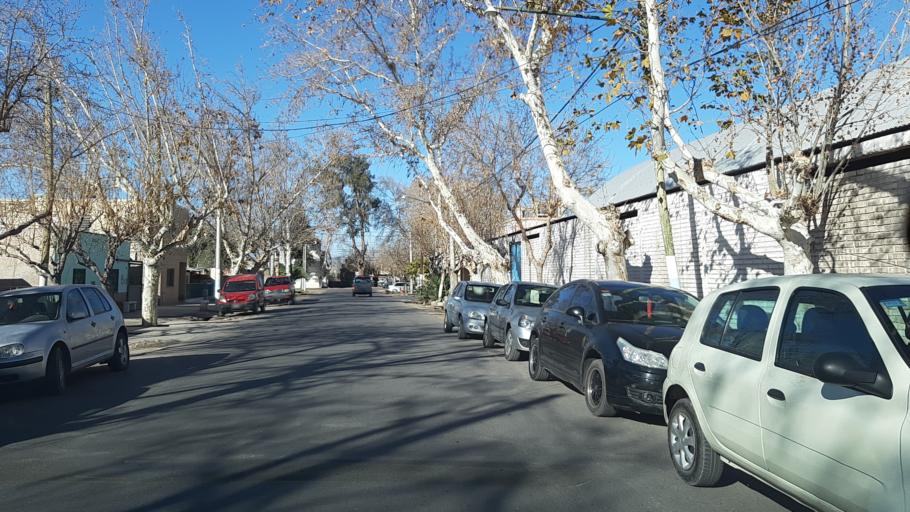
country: AR
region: San Juan
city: San Juan
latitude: -31.5401
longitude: -68.5684
